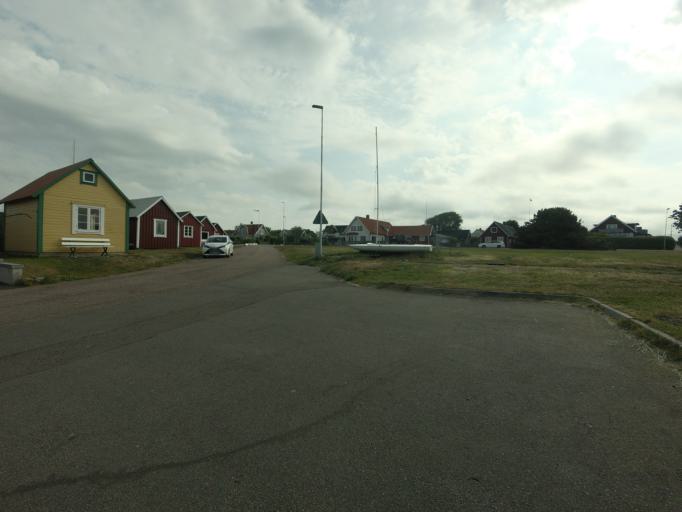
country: SE
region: Skane
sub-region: Angelholms Kommun
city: Vejbystrand
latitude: 56.3166
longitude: 12.7629
